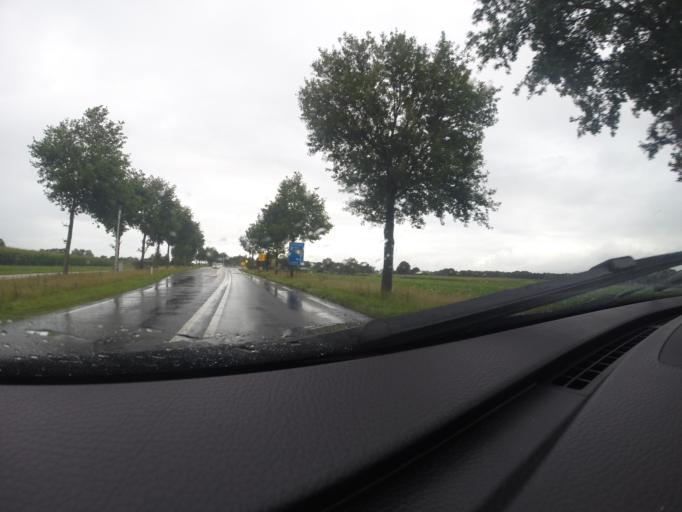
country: NL
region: Gelderland
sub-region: Gemeente Lochem
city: Laren
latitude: 52.1866
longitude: 6.3760
